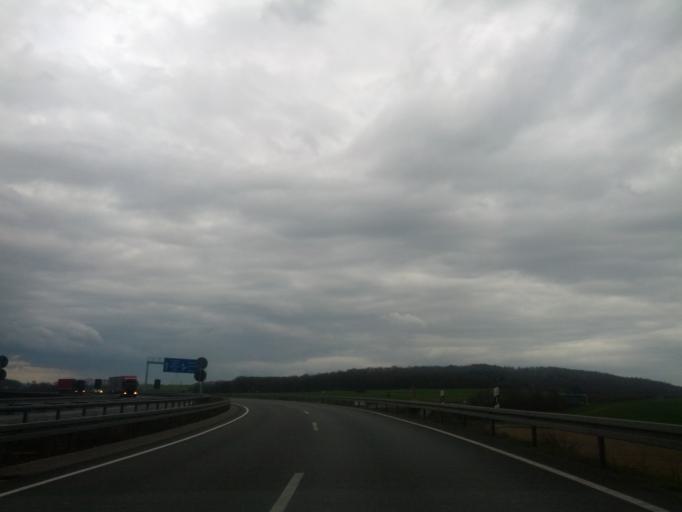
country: DE
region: Lower Saxony
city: Rosdorf
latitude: 51.4551
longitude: 9.8629
